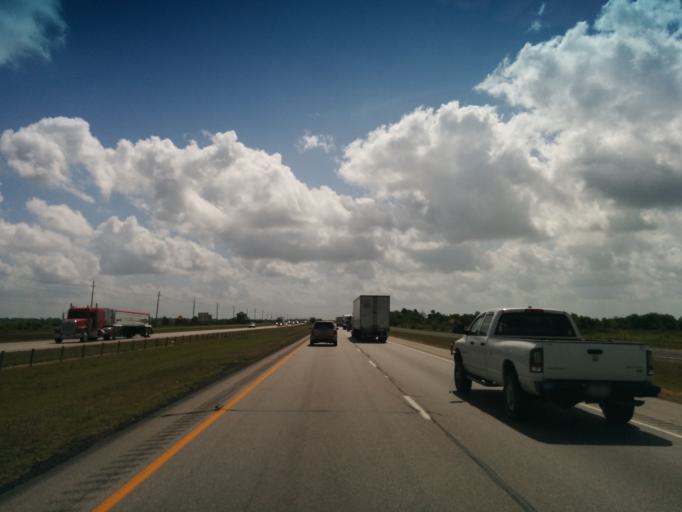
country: US
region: Texas
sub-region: Austin County
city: Sealy
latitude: 29.7603
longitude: -96.2106
